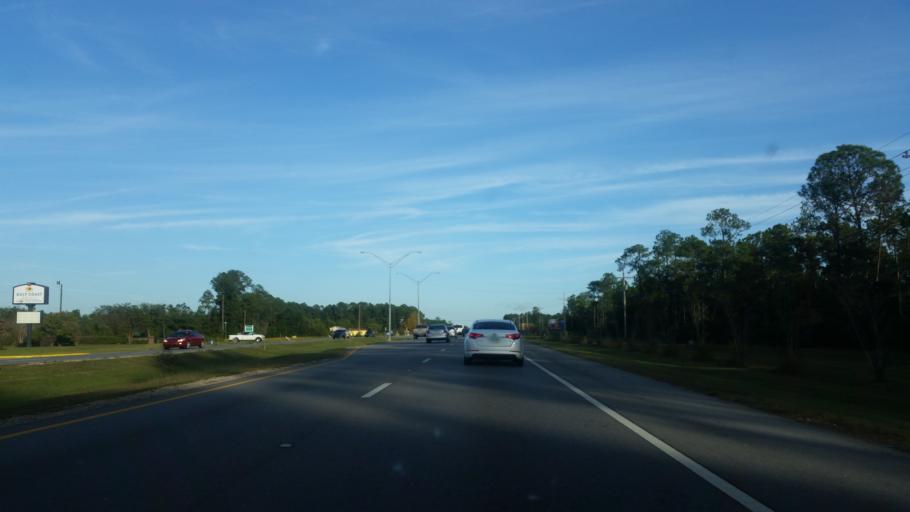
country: US
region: Mississippi
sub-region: Jackson County
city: Gulf Park Estates
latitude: 30.4063
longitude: -88.7435
